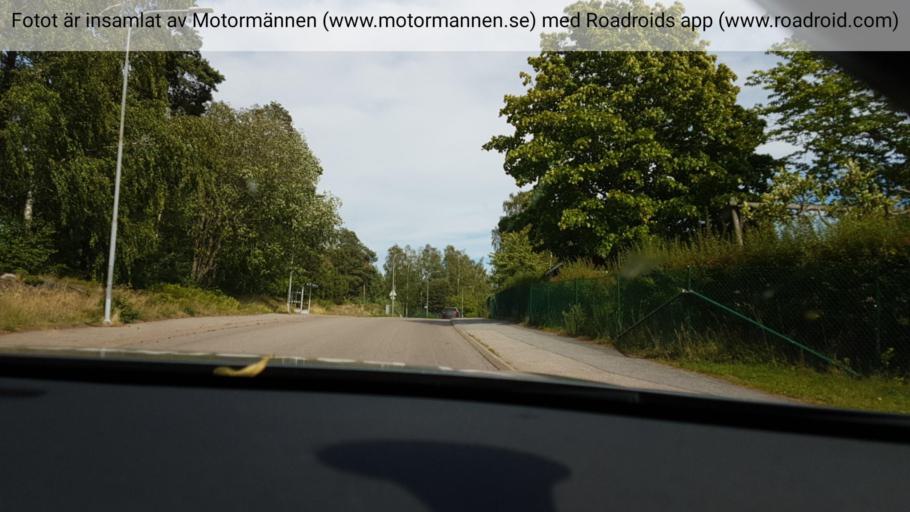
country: SE
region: Vaestra Goetaland
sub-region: Mariestads Kommun
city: Mariestad
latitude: 58.7157
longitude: 13.8473
